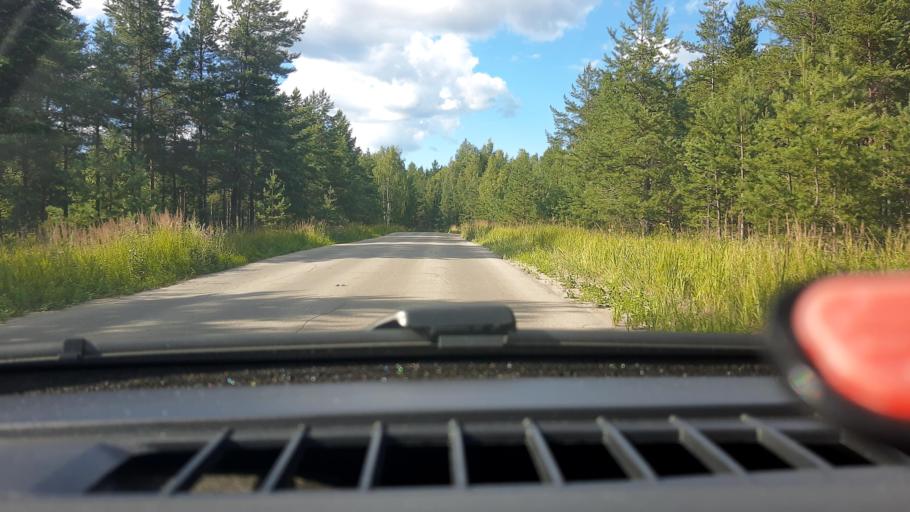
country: RU
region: Nizjnij Novgorod
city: Babino
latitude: 56.3106
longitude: 43.6300
